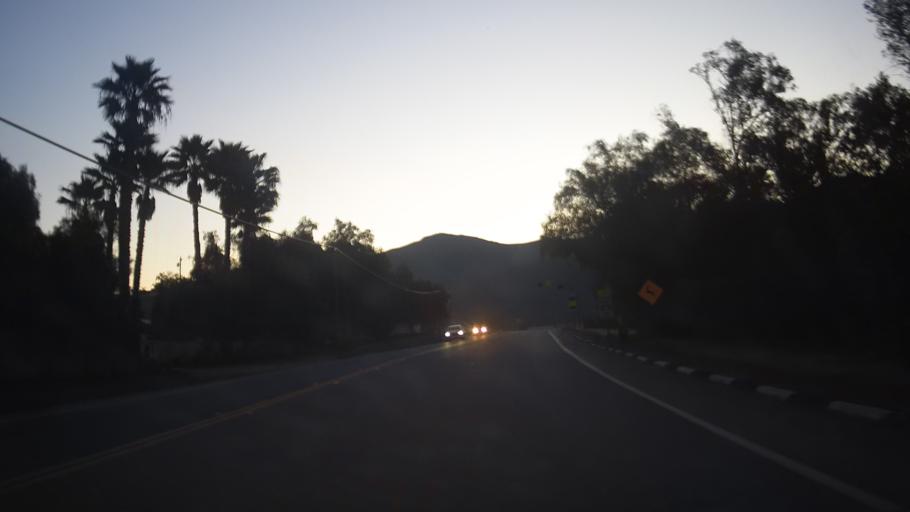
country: US
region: California
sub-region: San Diego County
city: Crest
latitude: 32.7819
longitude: -116.8542
